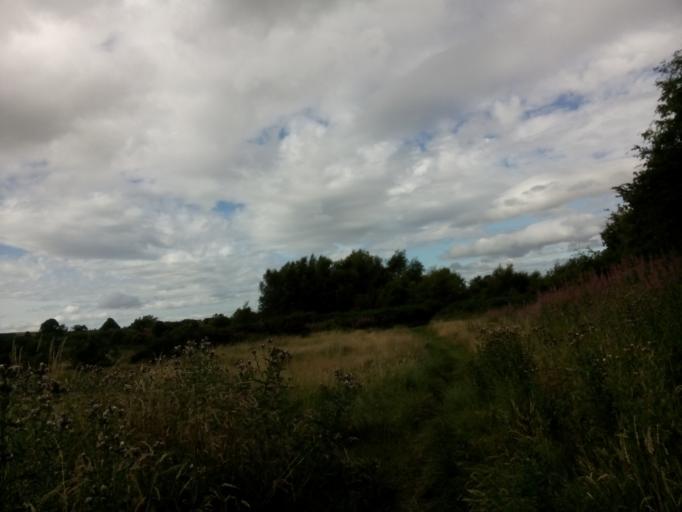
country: GB
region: England
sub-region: County Durham
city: Durham
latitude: 54.8007
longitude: -1.5834
